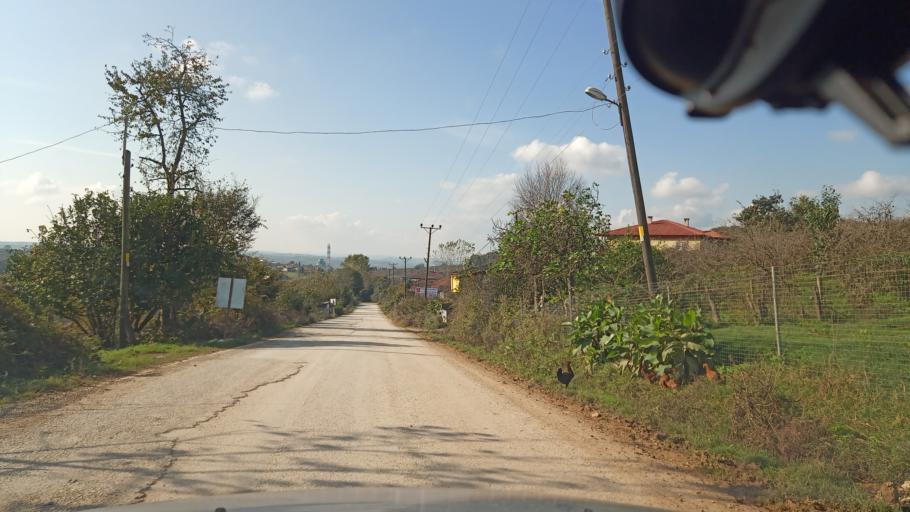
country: TR
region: Sakarya
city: Ferizli
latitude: 41.0970
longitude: 30.4653
